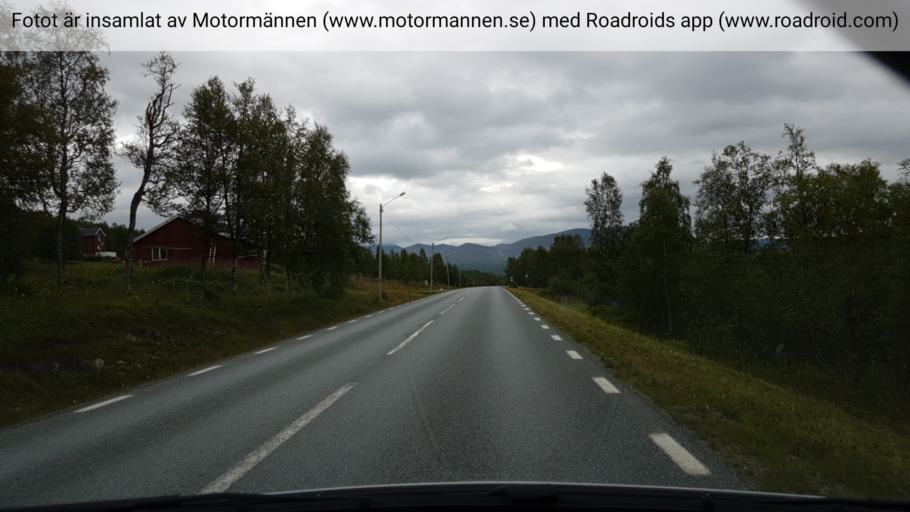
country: NO
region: Nordland
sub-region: Rana
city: Mo i Rana
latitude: 66.0414
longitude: 15.0001
